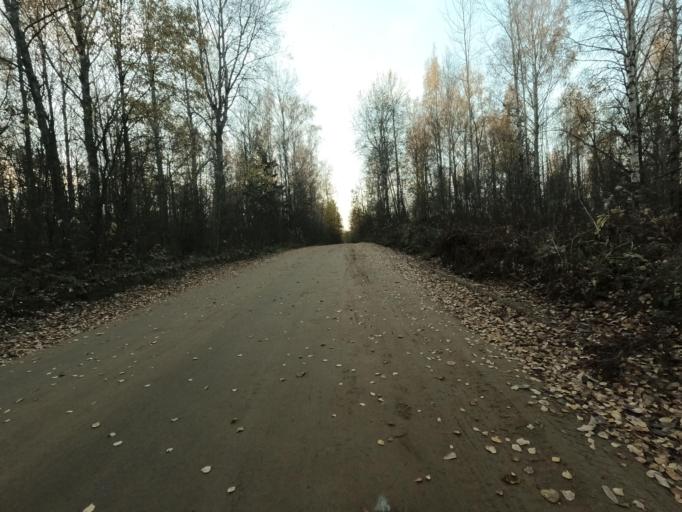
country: RU
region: Leningrad
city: Mga
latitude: 59.7547
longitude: 31.2817
